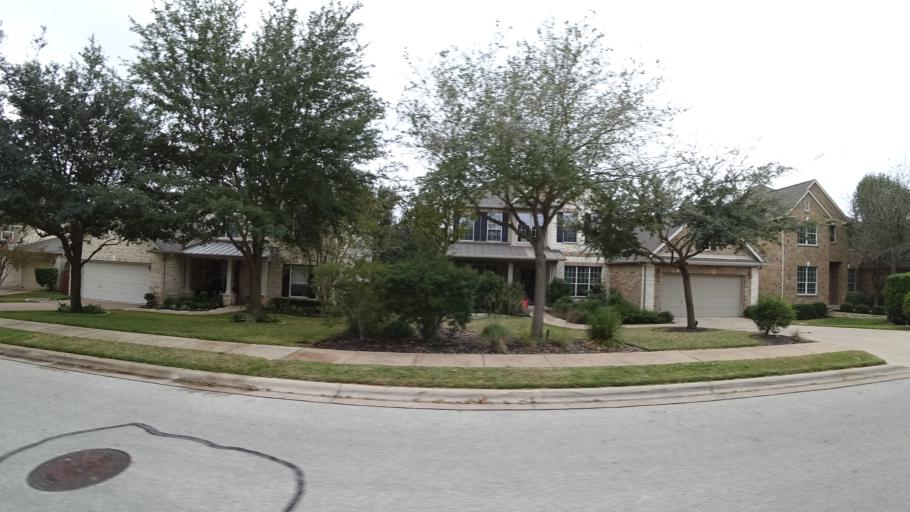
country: US
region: Texas
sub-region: Travis County
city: Hudson Bend
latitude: 30.3594
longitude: -97.8985
